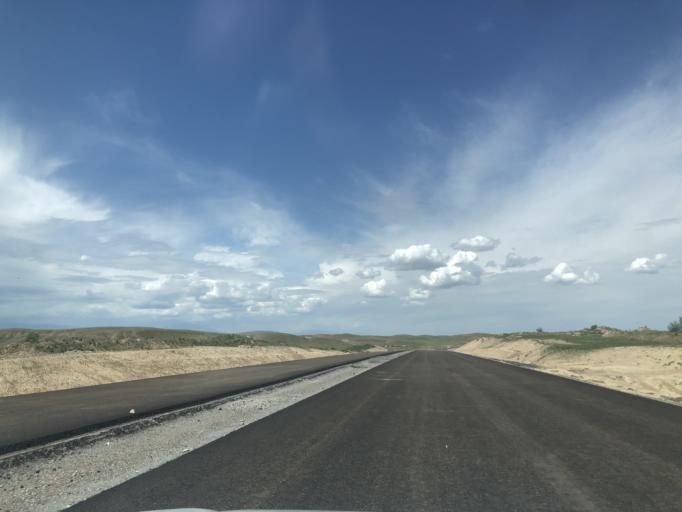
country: KG
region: Chuy
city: Bystrovka
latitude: 43.3006
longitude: 76.1226
